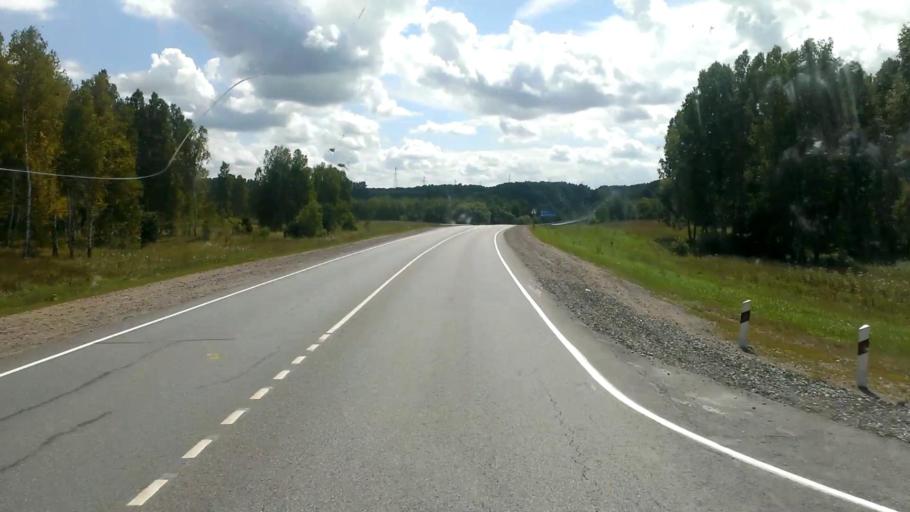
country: RU
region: Altai Krai
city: Troitskoye
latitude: 52.9392
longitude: 84.7841
